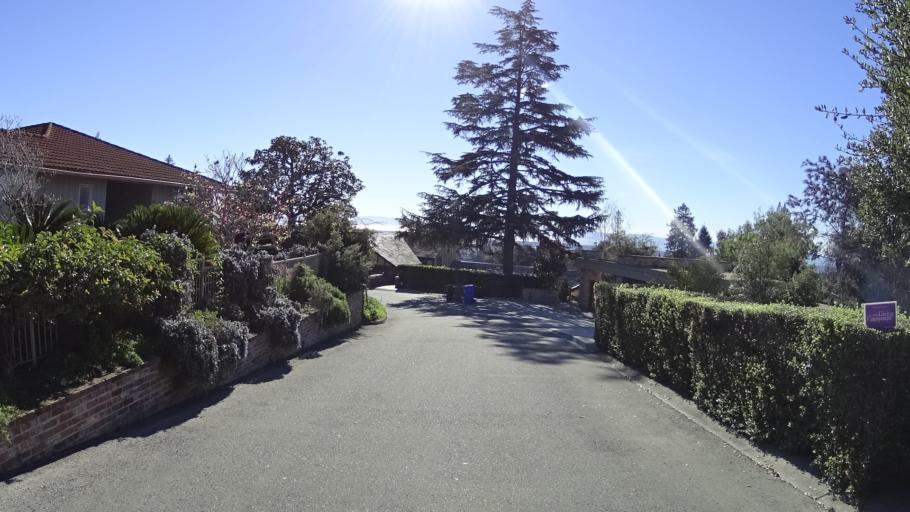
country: US
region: California
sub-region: Alameda County
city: Piedmont
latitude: 37.8227
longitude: -122.2172
